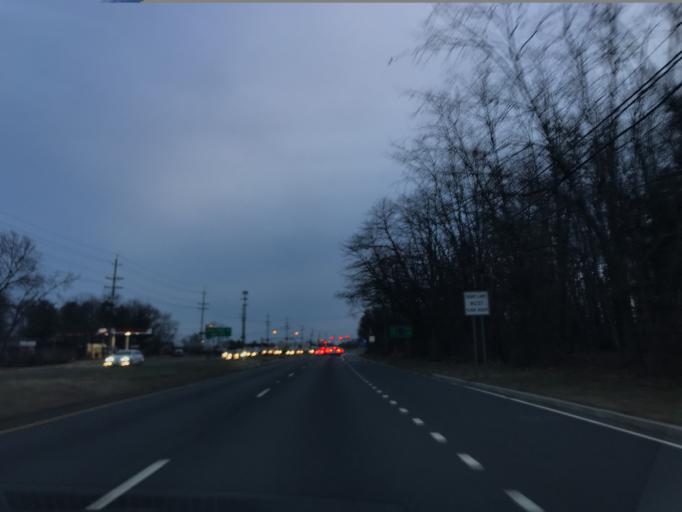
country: US
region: New Jersey
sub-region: Middlesex County
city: Dayton
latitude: 40.3817
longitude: -74.5026
